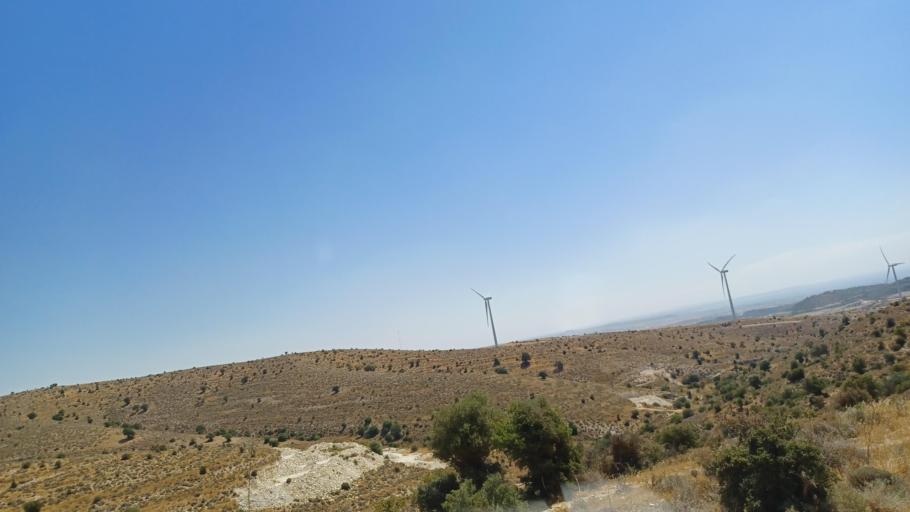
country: CY
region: Larnaka
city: Psevdas
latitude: 34.9633
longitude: 33.4806
